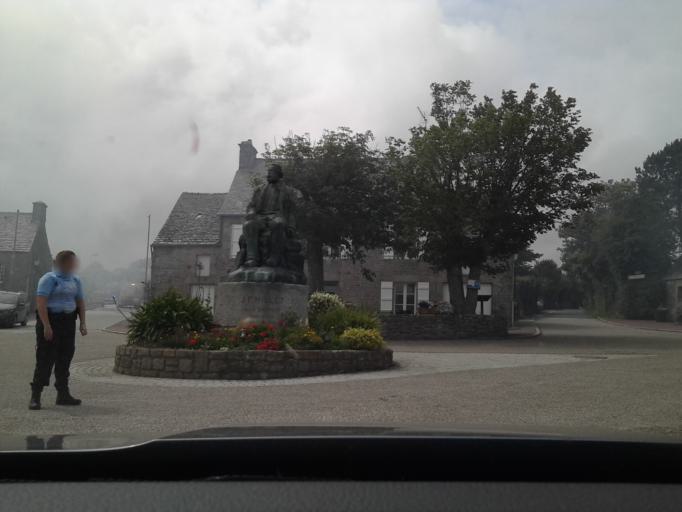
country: FR
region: Lower Normandy
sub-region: Departement de la Manche
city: Beaumont-Hague
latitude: 49.6748
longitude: -1.8008
